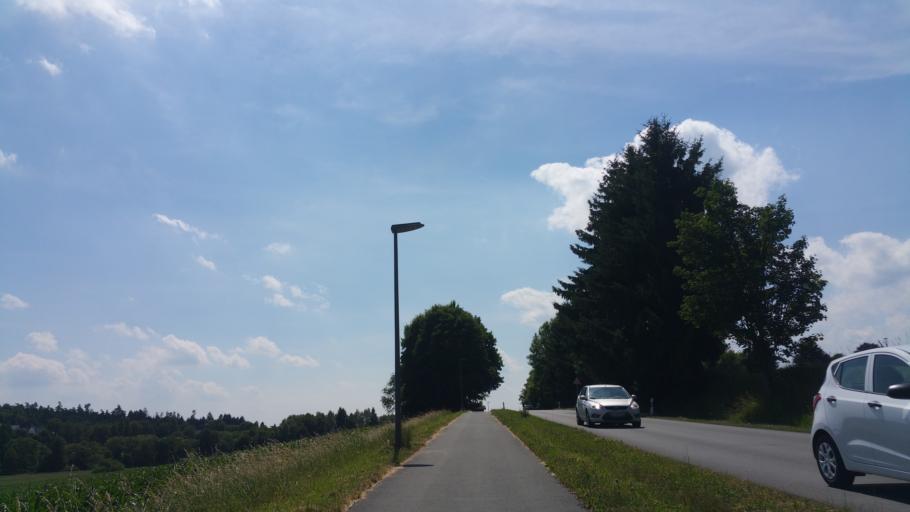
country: DE
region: Bavaria
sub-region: Upper Franconia
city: Schwarzenbach an der Saale
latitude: 50.2125
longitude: 11.9154
